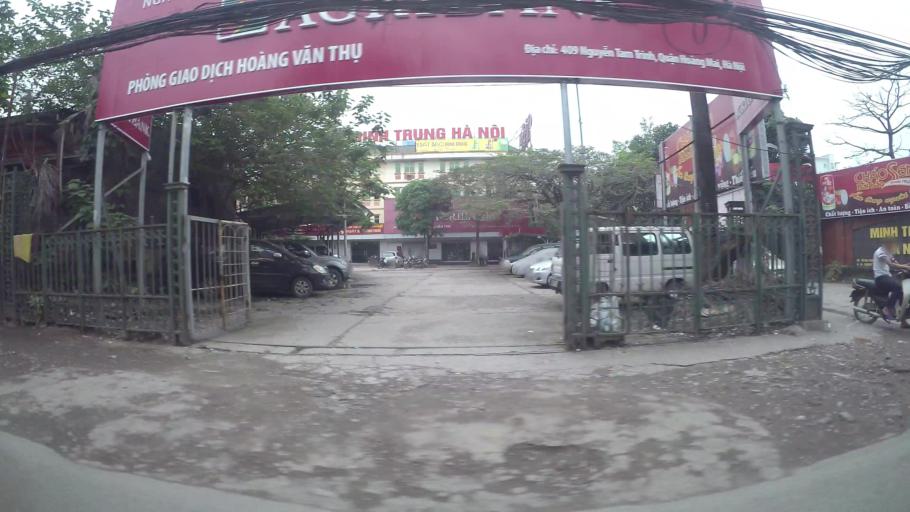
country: VN
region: Ha Noi
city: Hai BaTrung
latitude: 20.9853
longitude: 105.8637
